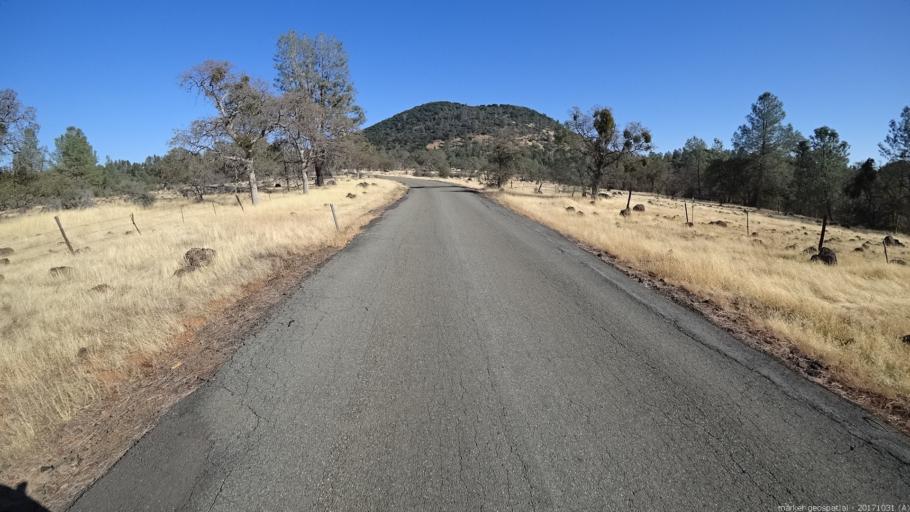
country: US
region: California
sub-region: Shasta County
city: Shingletown
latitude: 40.4577
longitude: -122.0148
